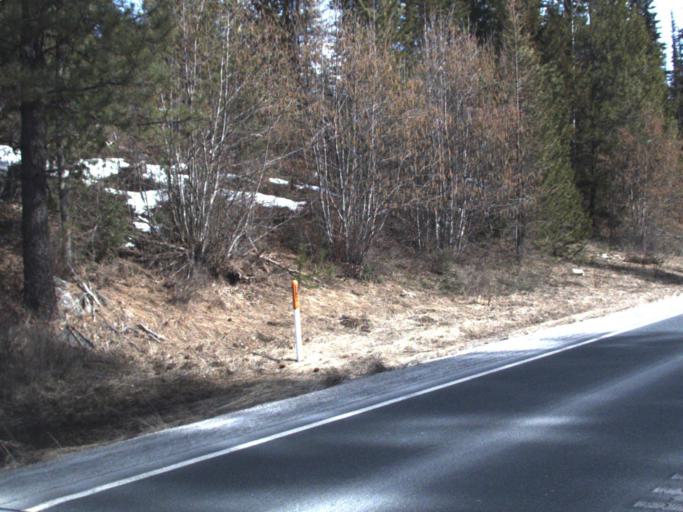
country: US
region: Washington
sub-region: Stevens County
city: Chewelah
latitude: 48.5334
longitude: -117.6140
